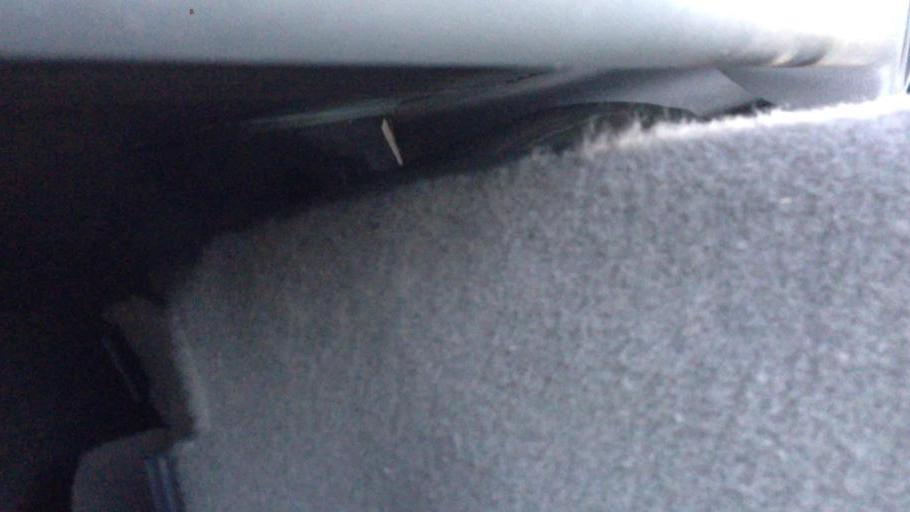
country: US
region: New York
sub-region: Columbia County
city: Hudson
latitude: 42.1954
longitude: -73.8071
